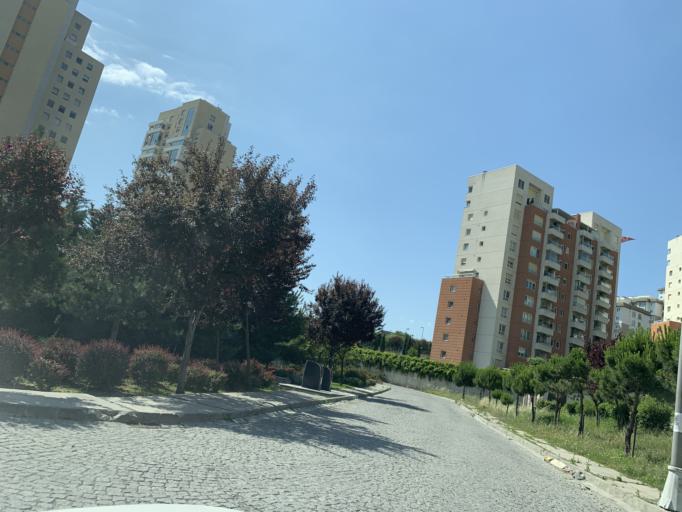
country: TR
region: Istanbul
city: Esenyurt
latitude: 41.0774
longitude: 28.6918
